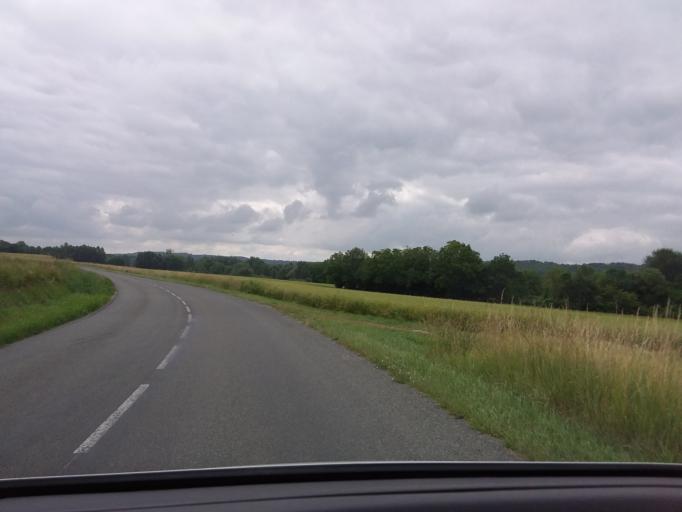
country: FR
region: Picardie
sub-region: Departement de l'Aisne
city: Vailly-sur-Aisne
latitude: 49.4050
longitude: 3.5394
